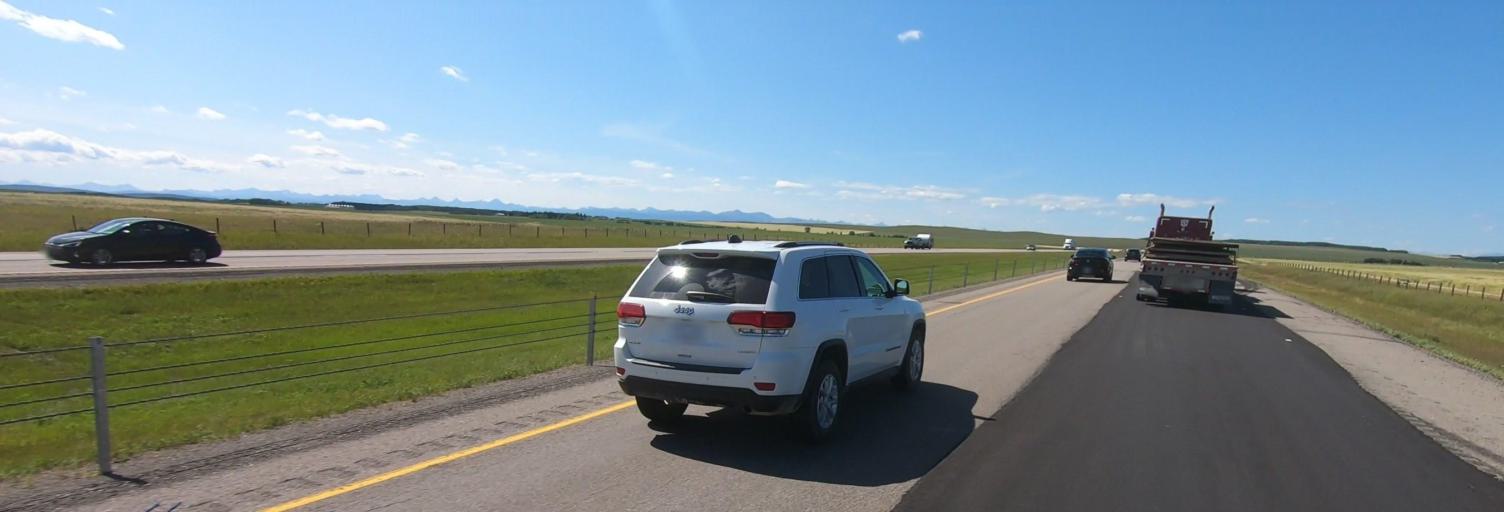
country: CA
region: Alberta
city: Cochrane
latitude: 51.0895
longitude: -114.3982
